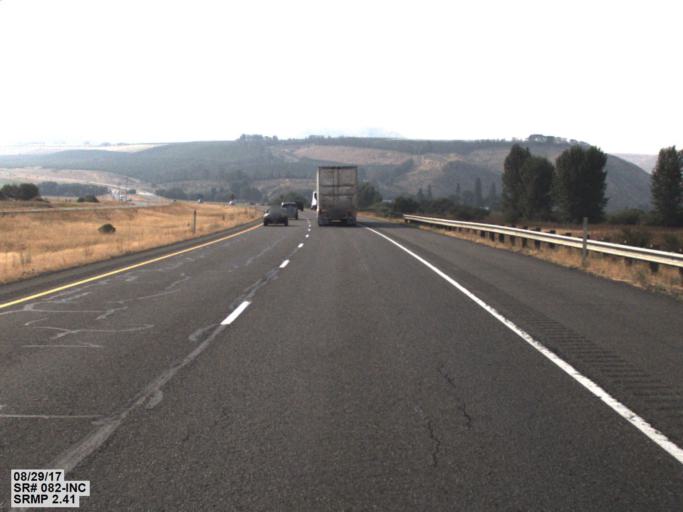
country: US
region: Washington
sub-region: Kittitas County
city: Ellensburg
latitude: 46.9367
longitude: -120.5067
